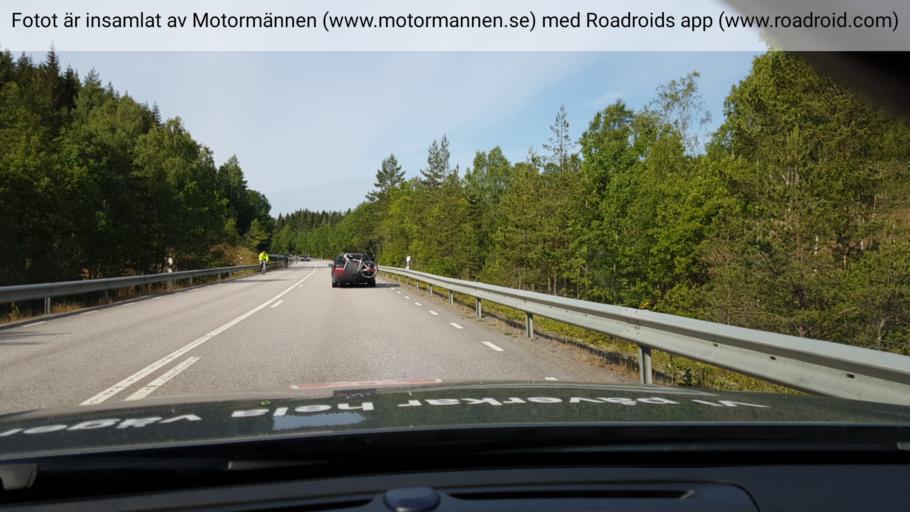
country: SE
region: Vaestra Goetaland
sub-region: Karlsborgs Kommun
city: Karlsborg
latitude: 58.6616
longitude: 14.5947
